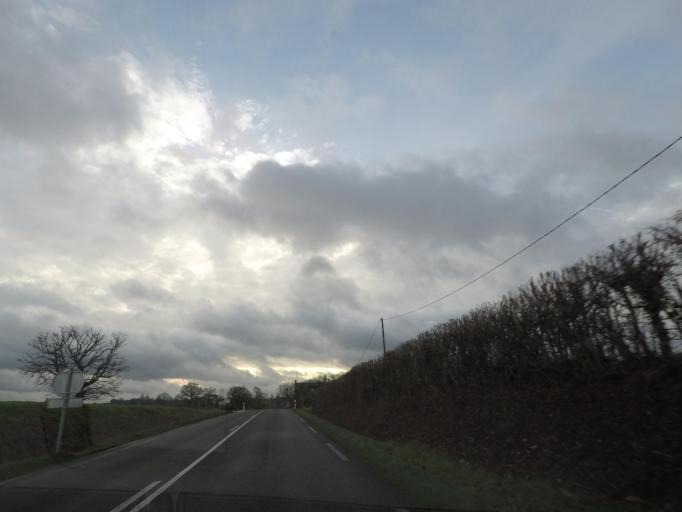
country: FR
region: Pays de la Loire
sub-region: Departement de la Sarthe
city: Cherre
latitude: 48.1301
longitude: 0.7000
